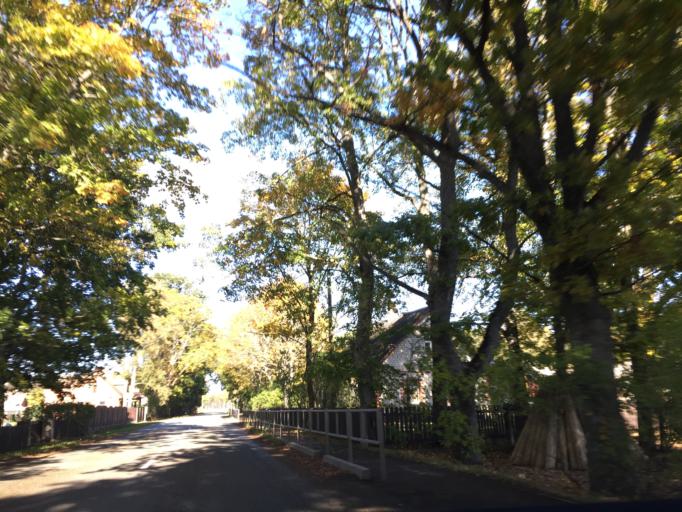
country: LV
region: Mesraga
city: Mersrags
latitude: 57.2525
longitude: 23.1734
